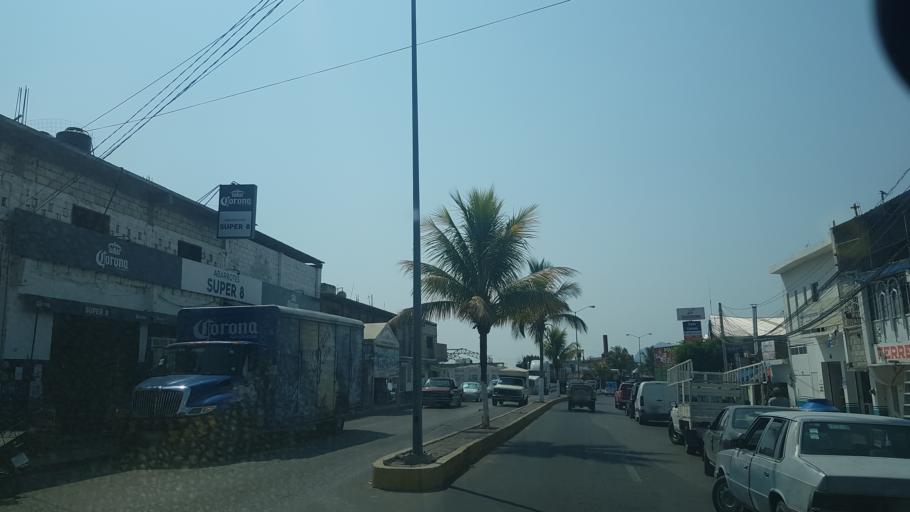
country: MX
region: Morelos
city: Amayuca
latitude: 18.7227
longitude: -98.7947
